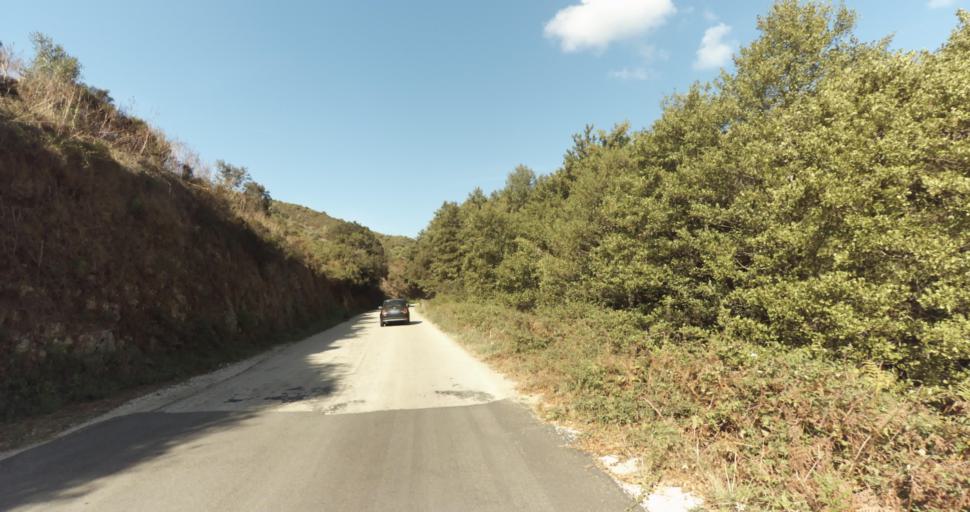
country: FR
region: Corsica
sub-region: Departement de la Corse-du-Sud
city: Ajaccio
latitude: 41.9331
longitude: 8.6888
